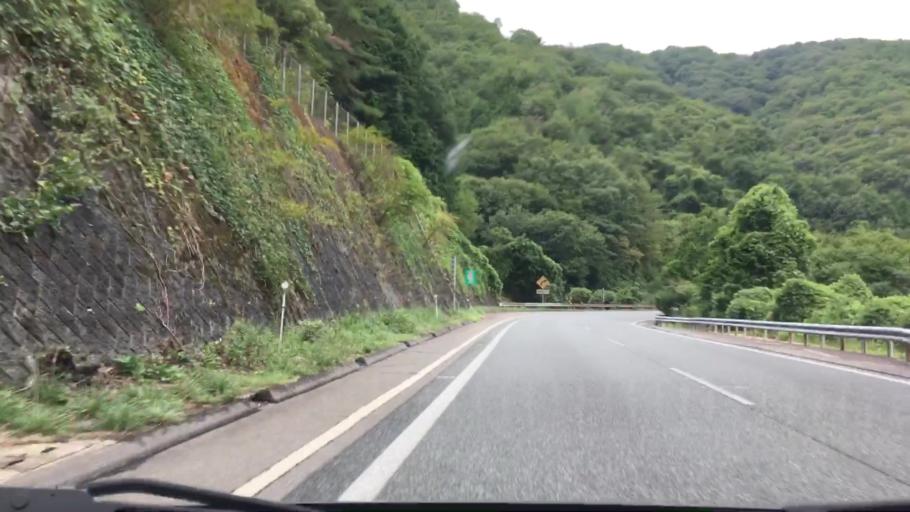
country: JP
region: Okayama
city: Niimi
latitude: 34.9864
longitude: 133.6090
